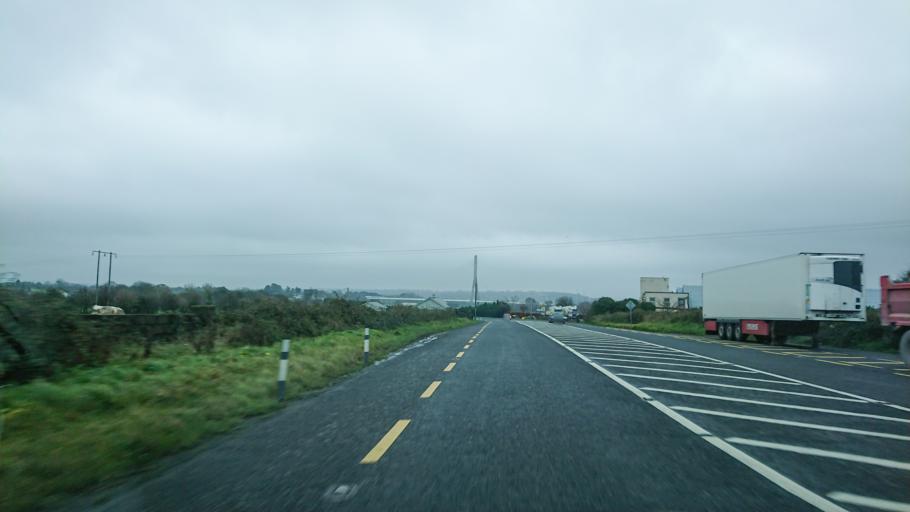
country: IE
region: Munster
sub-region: Waterford
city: Waterford
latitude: 52.2808
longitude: -7.1694
